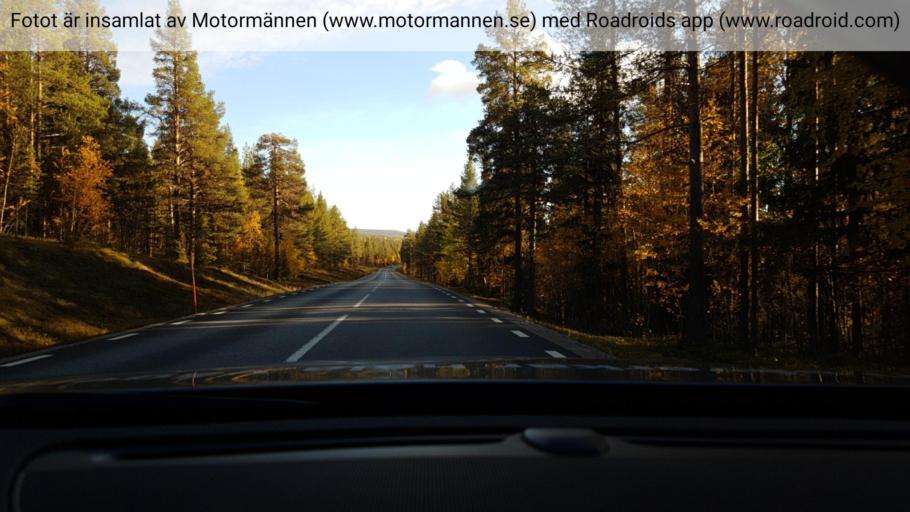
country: SE
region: Norrbotten
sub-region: Jokkmokks Kommun
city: Jokkmokk
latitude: 66.9258
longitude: 19.8249
